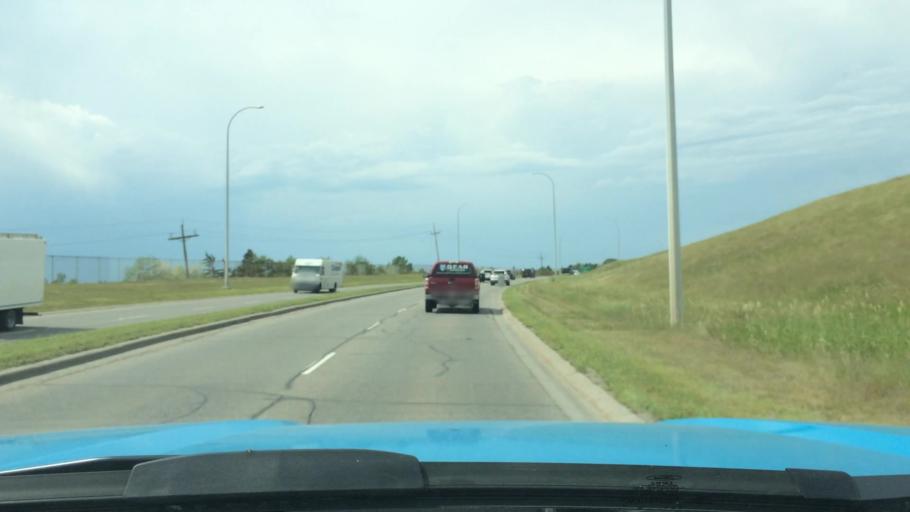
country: CA
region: Alberta
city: Calgary
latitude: 51.0939
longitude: -114.1109
